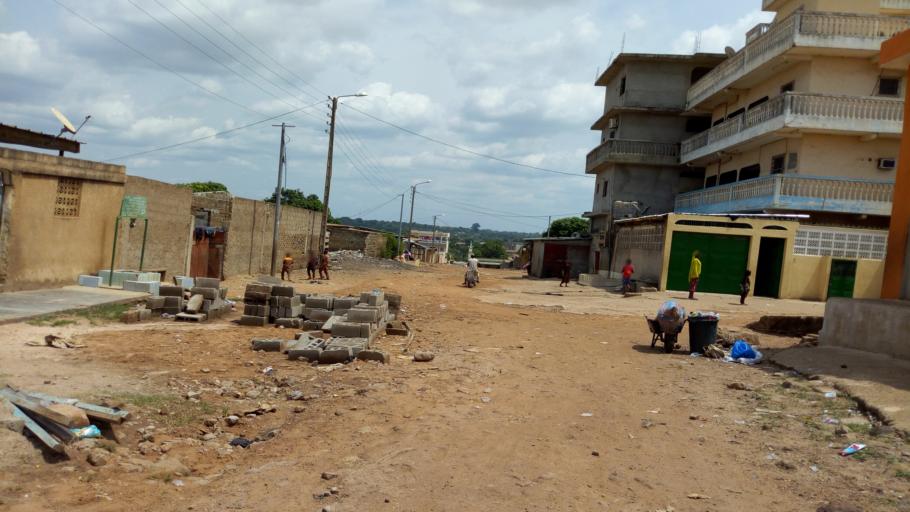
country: CI
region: Vallee du Bandama
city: Bouake
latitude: 7.7170
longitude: -5.0243
